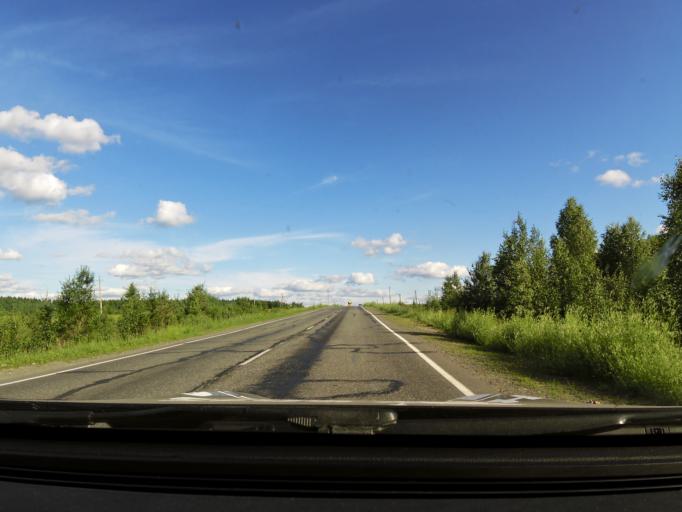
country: RU
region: Kirov
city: Omutninsk
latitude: 58.6910
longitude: 52.1323
